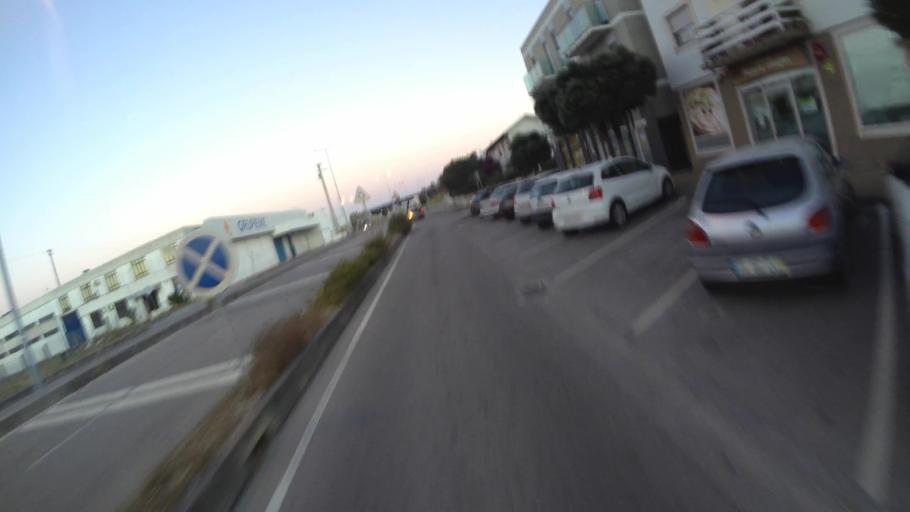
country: PT
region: Aveiro
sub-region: Ilhavo
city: Gafanha da Nazare
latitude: 40.6325
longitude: -8.6902
